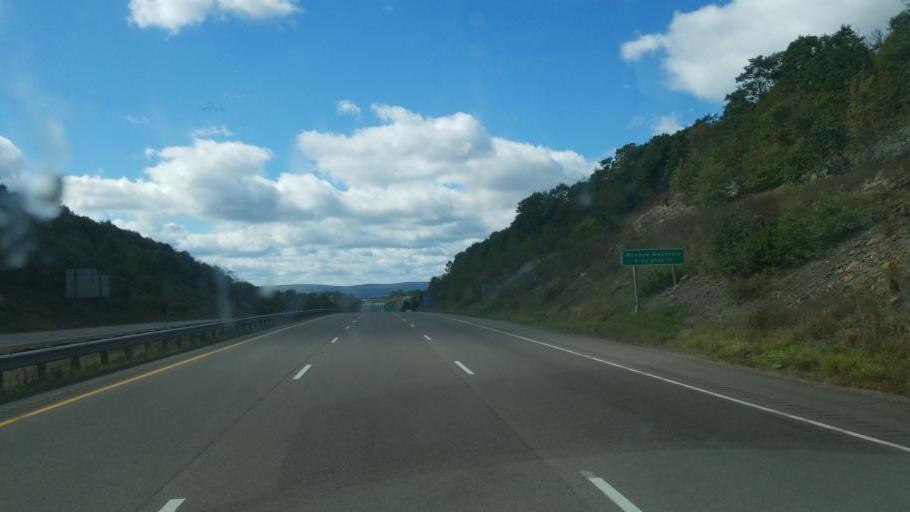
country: US
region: Pennsylvania
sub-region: Somerset County
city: Meyersdale
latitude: 39.6856
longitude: -79.0876
